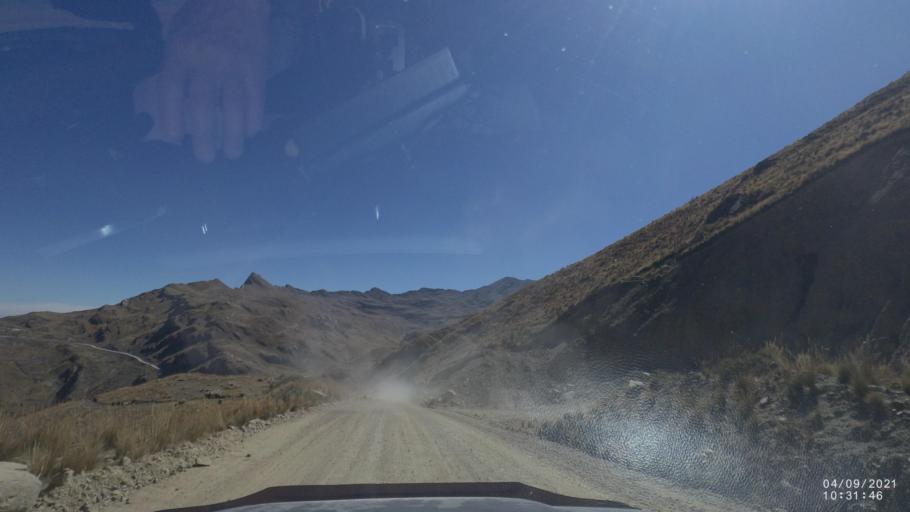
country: BO
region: Cochabamba
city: Sipe Sipe
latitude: -17.3000
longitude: -66.4462
